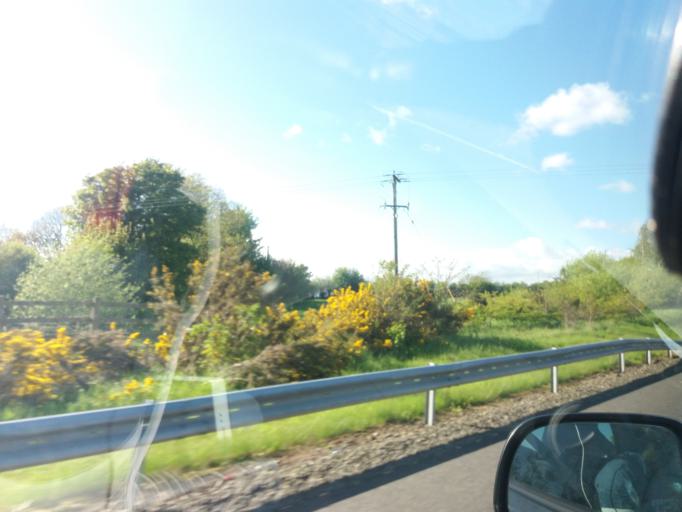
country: IE
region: Munster
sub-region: Waterford
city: Waterford
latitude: 52.3080
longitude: -7.1415
